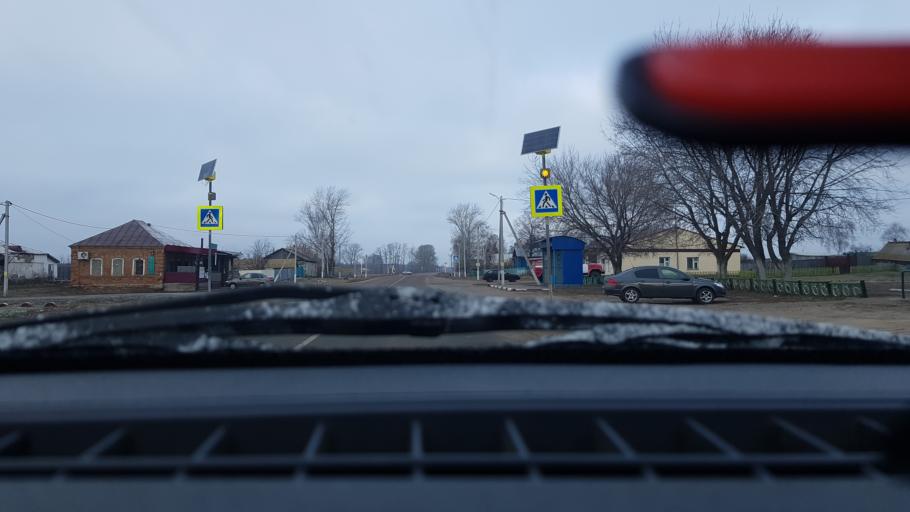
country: RU
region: Tatarstan
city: Kuybyshevskiy Zaton
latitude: 54.9123
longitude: 49.4851
